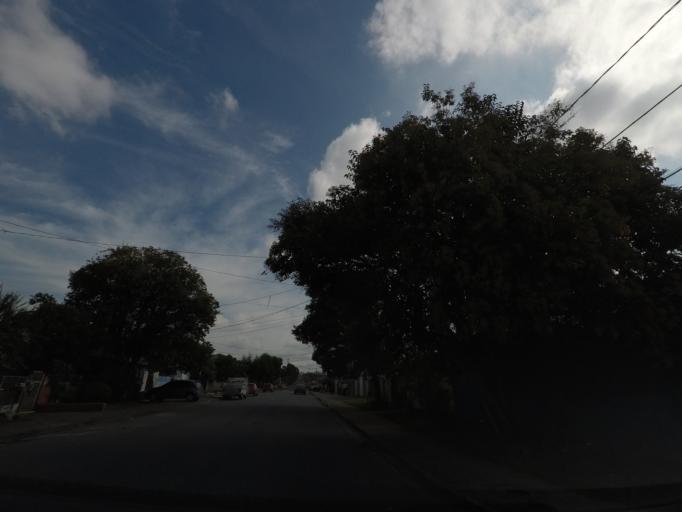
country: BR
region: Parana
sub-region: Curitiba
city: Curitiba
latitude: -25.4799
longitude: -49.2738
